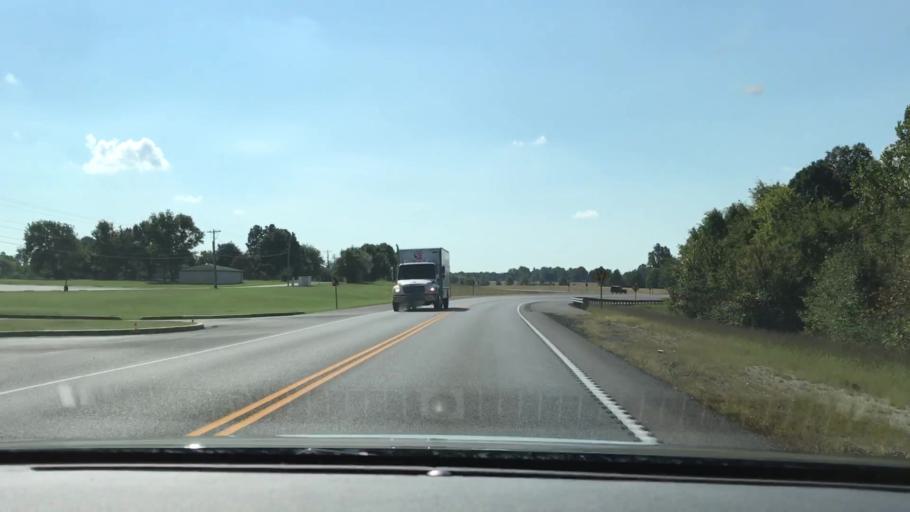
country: US
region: Kentucky
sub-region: Marshall County
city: Benton
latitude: 36.8171
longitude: -88.3500
